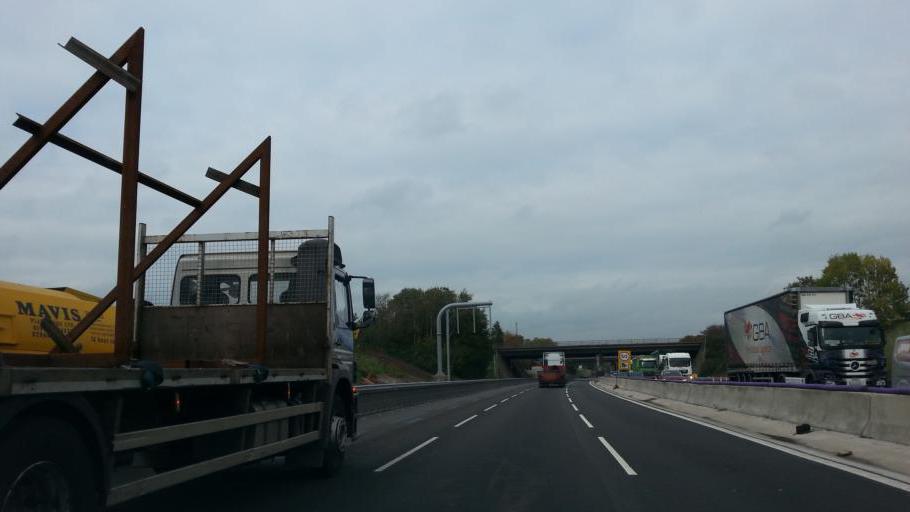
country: GB
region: England
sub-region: Cheshire East
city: Holmes Chapel
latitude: 53.1983
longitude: -2.3869
